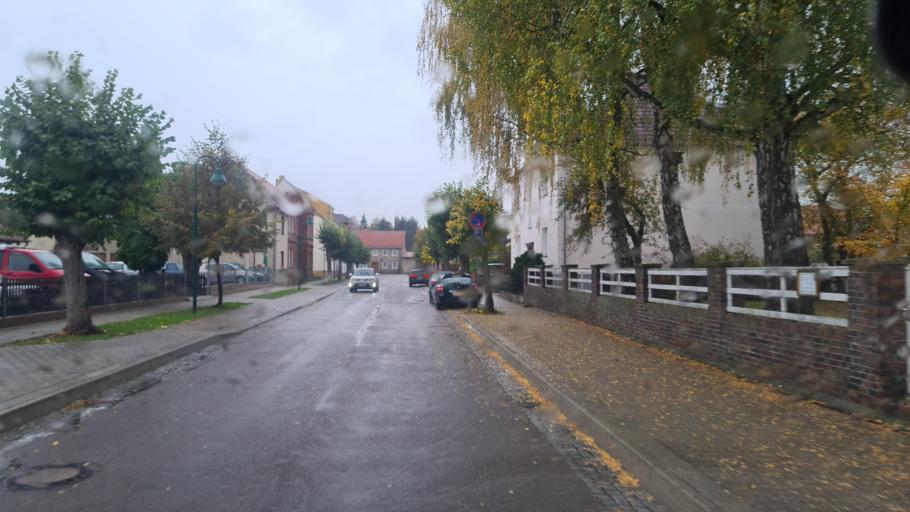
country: DE
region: Brandenburg
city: Schlieben
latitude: 51.7257
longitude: 13.3822
